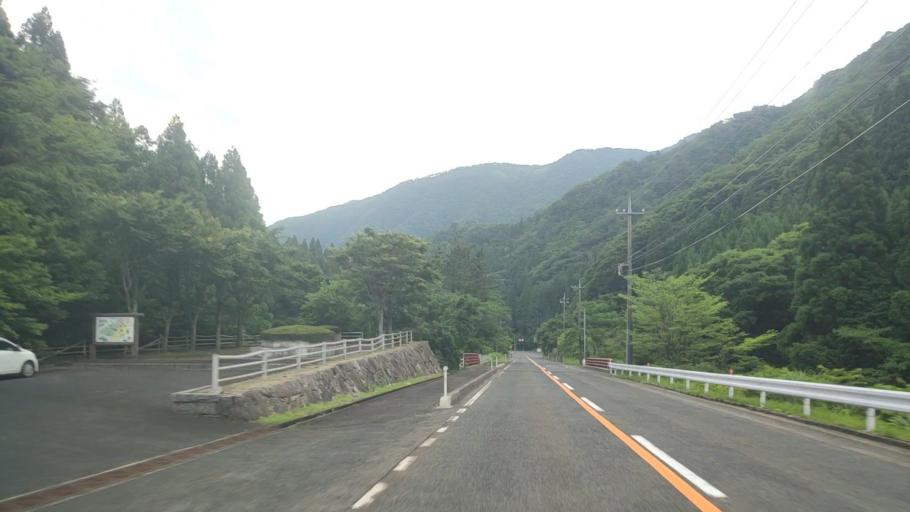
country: JP
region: Tottori
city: Kurayoshi
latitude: 35.3160
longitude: 133.9000
